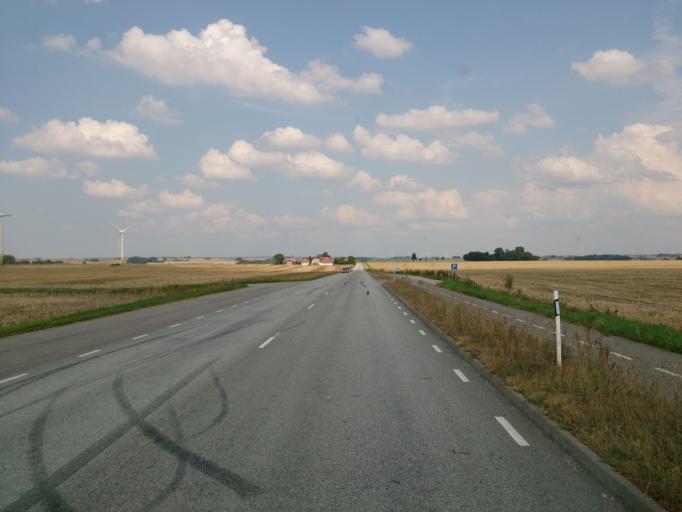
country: SE
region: Skane
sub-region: Eslovs Kommun
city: Eslov
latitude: 55.7512
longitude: 13.2957
